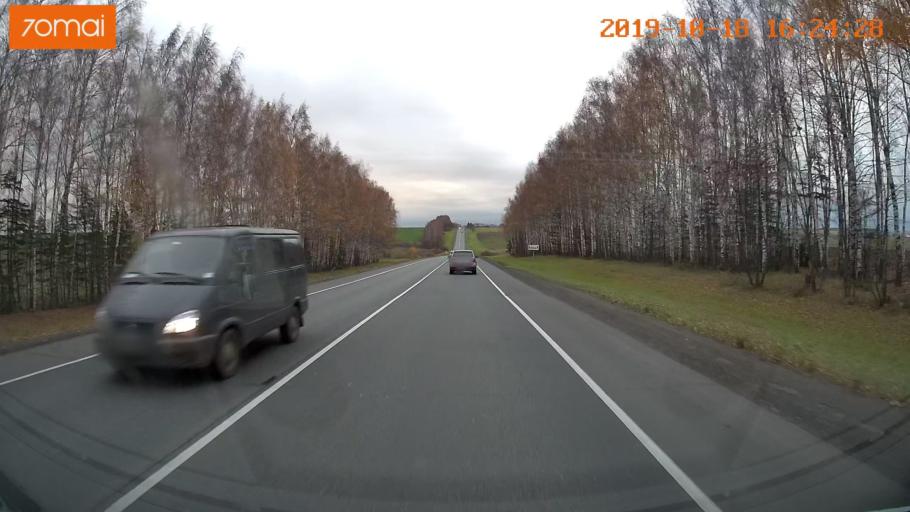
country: RU
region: Vladimir
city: Bogolyubovo
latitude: 56.2635
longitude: 40.4645
